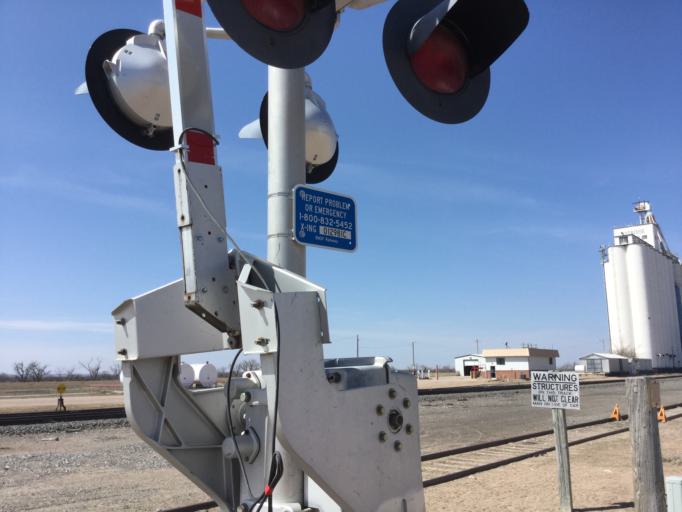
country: US
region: Kansas
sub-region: Hamilton County
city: Syracuse
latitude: 37.9335
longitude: -101.5464
